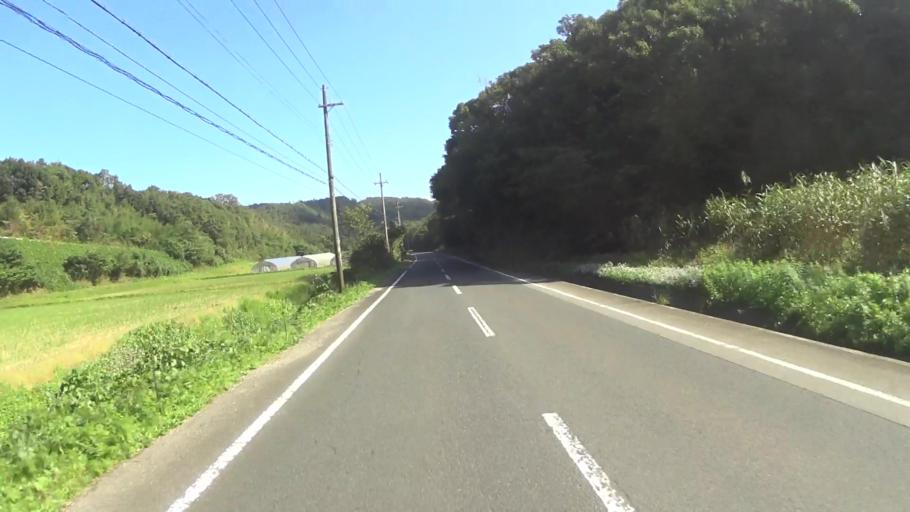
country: JP
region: Kyoto
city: Miyazu
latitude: 35.7054
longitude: 135.0770
